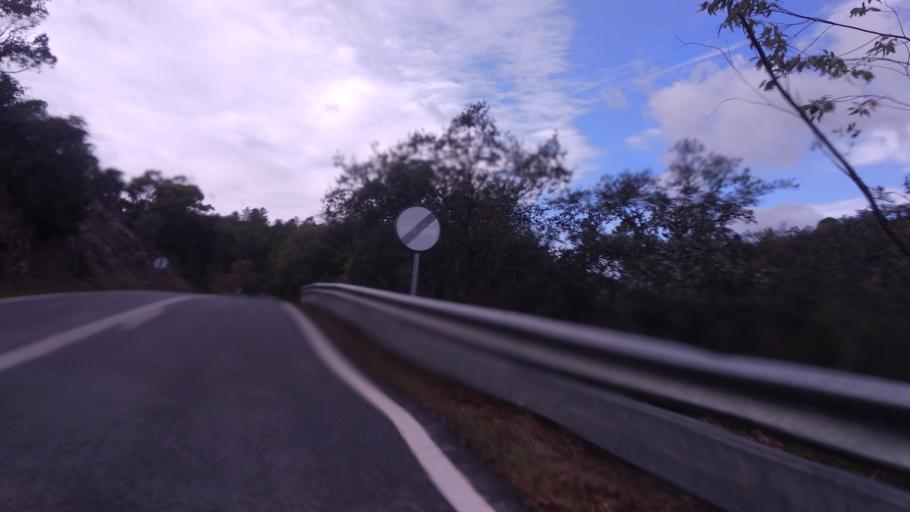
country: PT
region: Faro
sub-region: Sao Bras de Alportel
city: Sao Bras de Alportel
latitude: 37.1805
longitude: -7.9148
